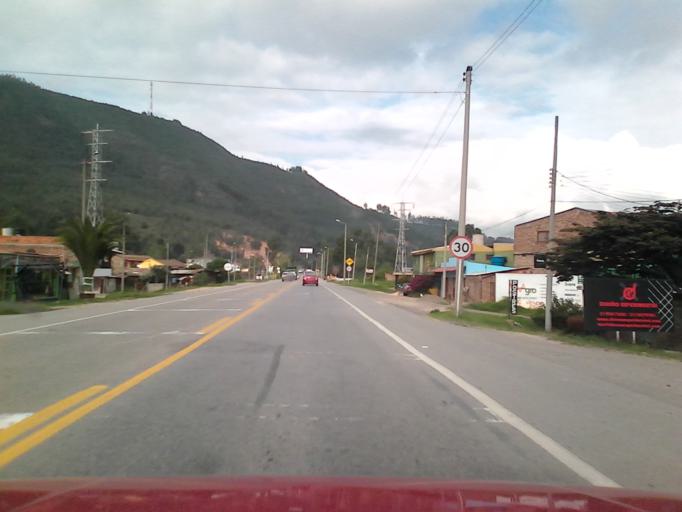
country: CO
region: Boyaca
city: Tibasosa
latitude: 5.7937
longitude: -72.9918
